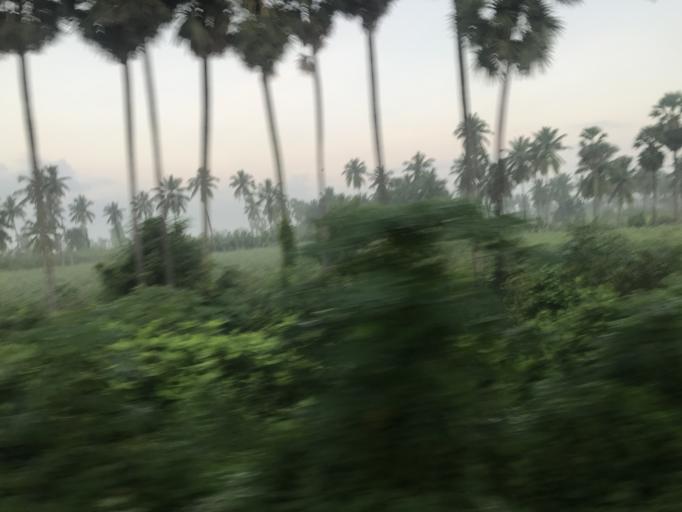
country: IN
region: Andhra Pradesh
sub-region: Guntur
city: Ponnur
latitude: 16.0791
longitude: 80.5625
